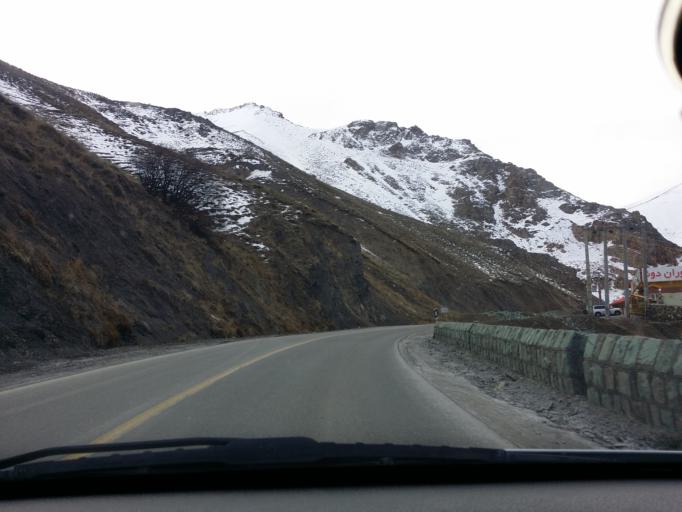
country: IR
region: Tehran
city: Tajrish
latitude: 36.1803
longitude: 51.3188
